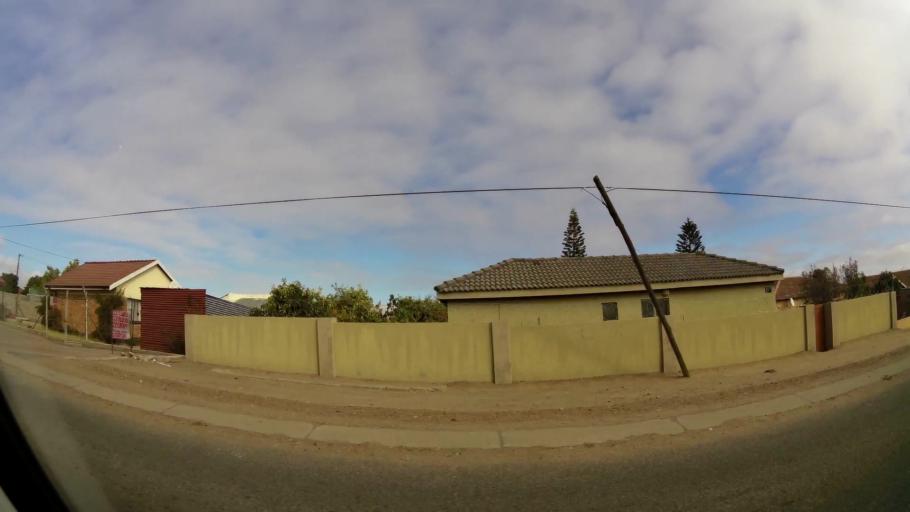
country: ZA
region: Limpopo
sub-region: Capricorn District Municipality
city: Polokwane
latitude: -23.8426
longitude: 29.3805
